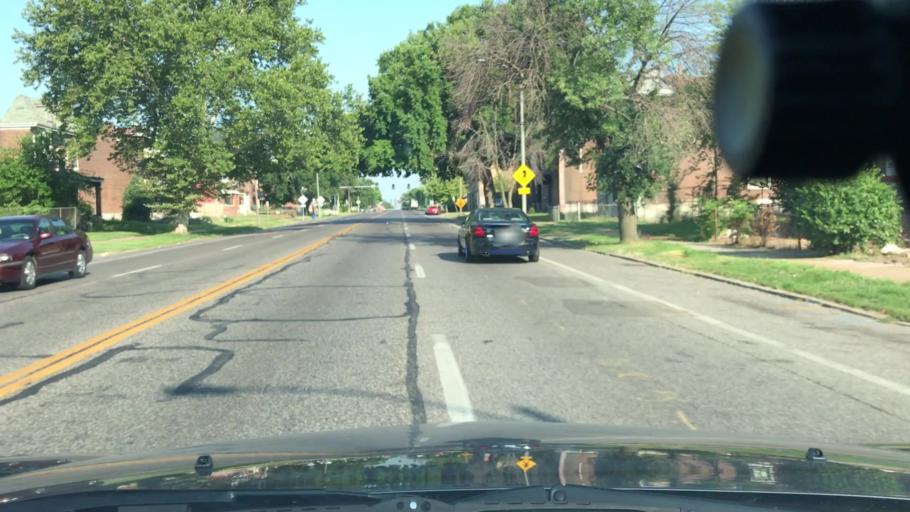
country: US
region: Missouri
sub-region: Saint Louis County
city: Hillsdale
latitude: 38.6577
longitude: -90.2543
